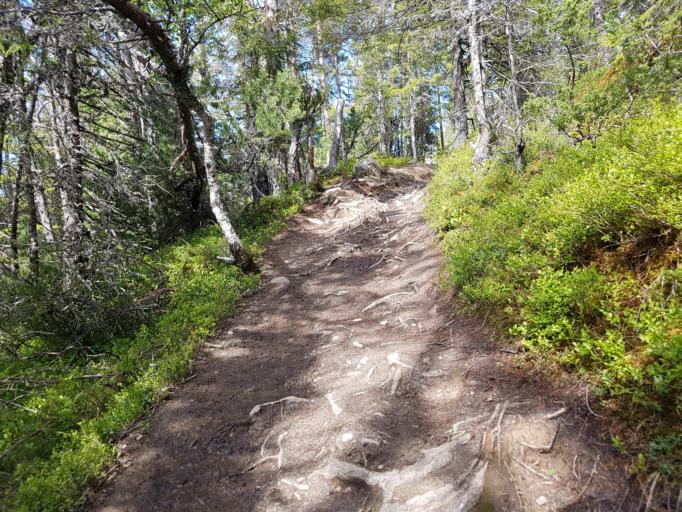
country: NO
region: Sor-Trondelag
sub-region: Trondheim
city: Trondheim
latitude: 63.4301
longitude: 10.3052
